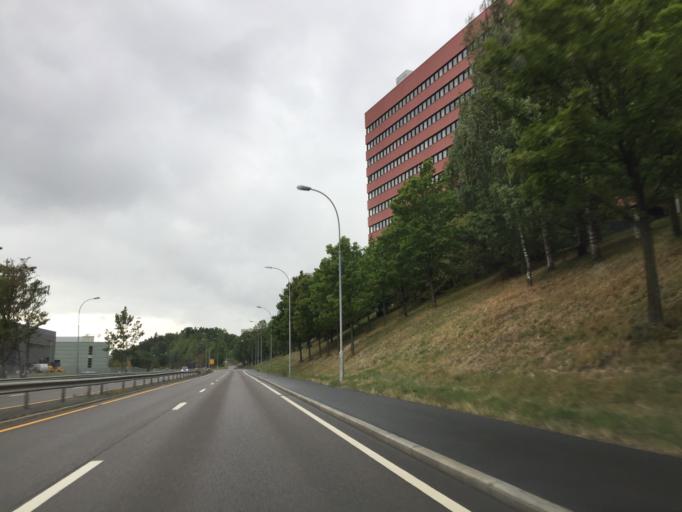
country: NO
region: Oslo
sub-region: Oslo
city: Oslo
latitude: 59.9394
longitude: 10.8455
